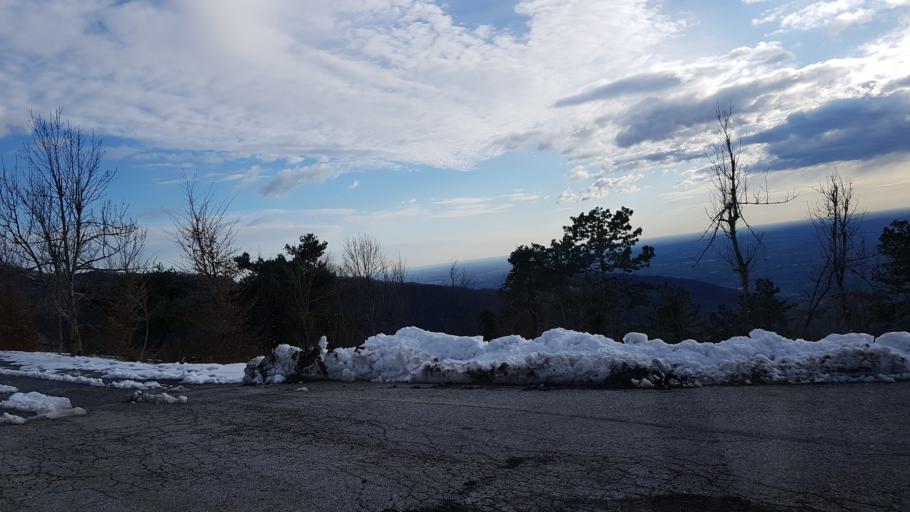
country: IT
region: Friuli Venezia Giulia
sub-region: Provincia di Udine
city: Faedis
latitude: 46.1814
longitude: 13.3933
